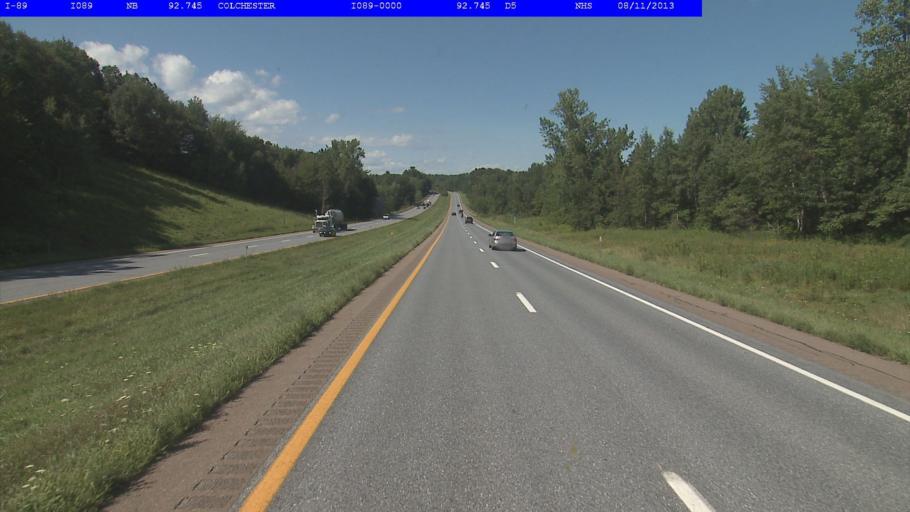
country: US
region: Vermont
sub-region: Chittenden County
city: Winooski
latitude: 44.5204
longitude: -73.1925
